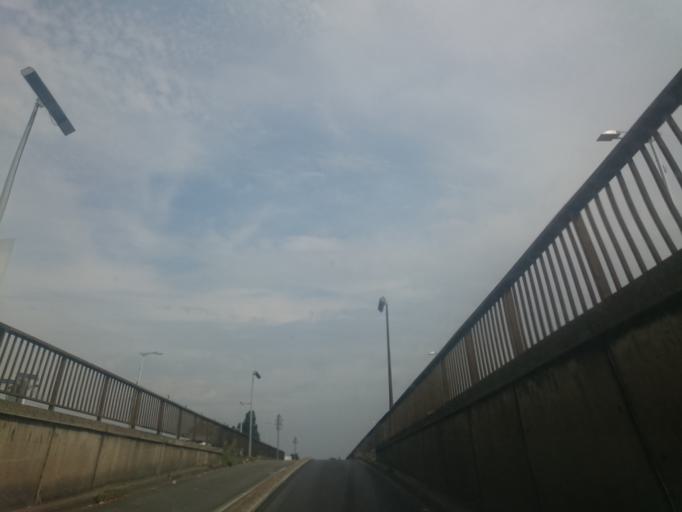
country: FR
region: Ile-de-France
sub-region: Departement de l'Essonne
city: Paray-Vieille-Poste
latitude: 48.7135
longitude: 2.3712
